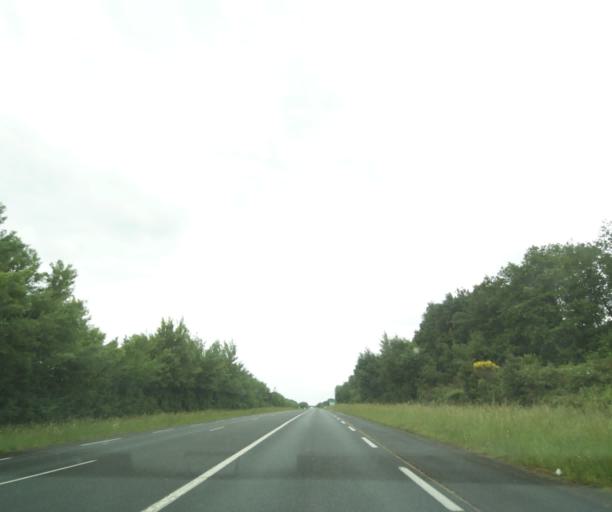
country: FR
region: Poitou-Charentes
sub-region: Departement des Deux-Sevres
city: Airvault
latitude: 46.7942
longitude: -0.2137
